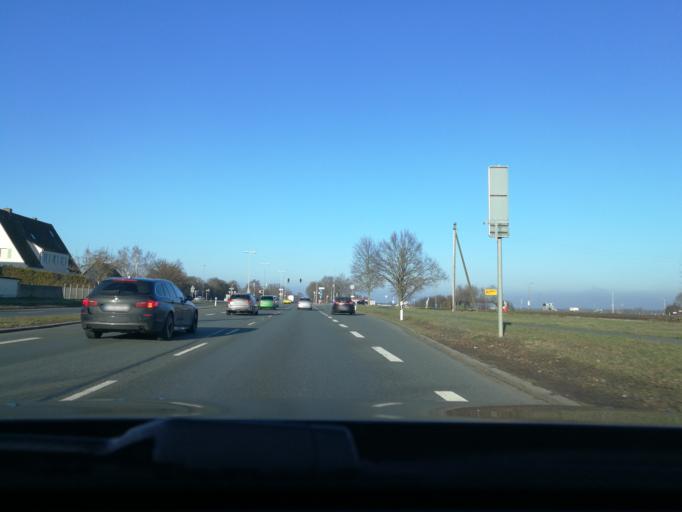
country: DE
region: Bavaria
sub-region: Regierungsbezirk Mittelfranken
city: Wetzendorf
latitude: 49.5018
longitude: 11.0464
